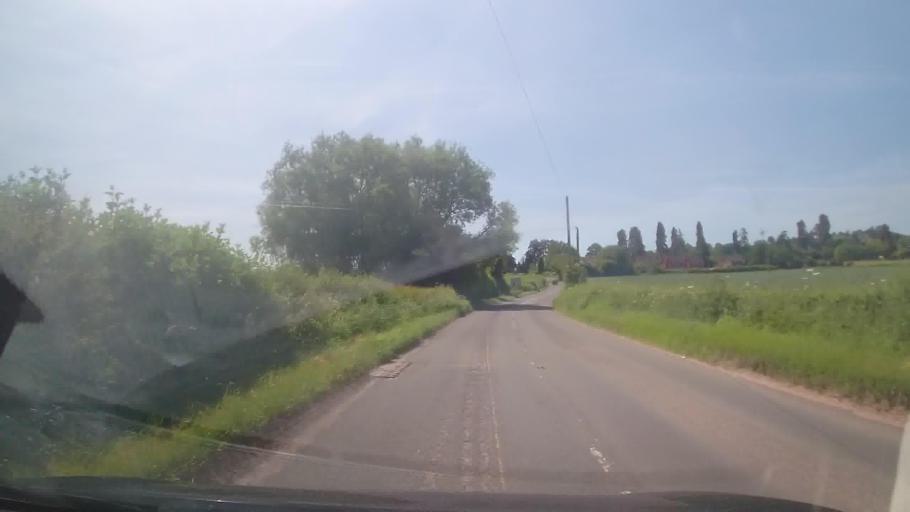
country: GB
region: England
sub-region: Herefordshire
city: Much Birch
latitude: 51.9717
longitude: -2.7397
